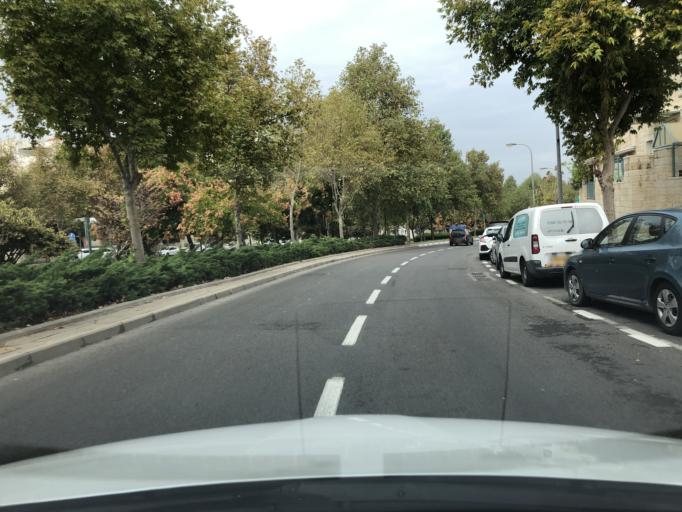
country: IL
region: Central District
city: Modiin
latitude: 31.9144
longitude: 35.0053
